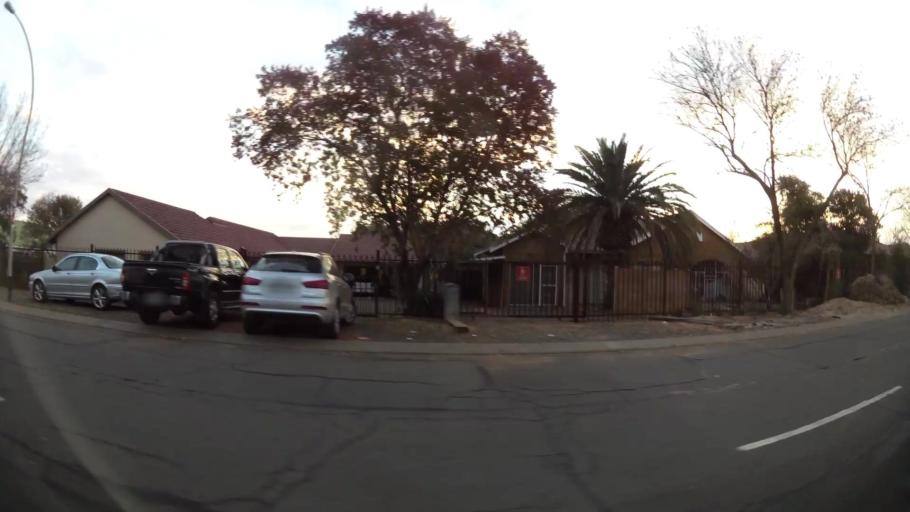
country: ZA
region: Orange Free State
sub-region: Mangaung Metropolitan Municipality
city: Bloemfontein
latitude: -29.1667
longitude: 26.1847
